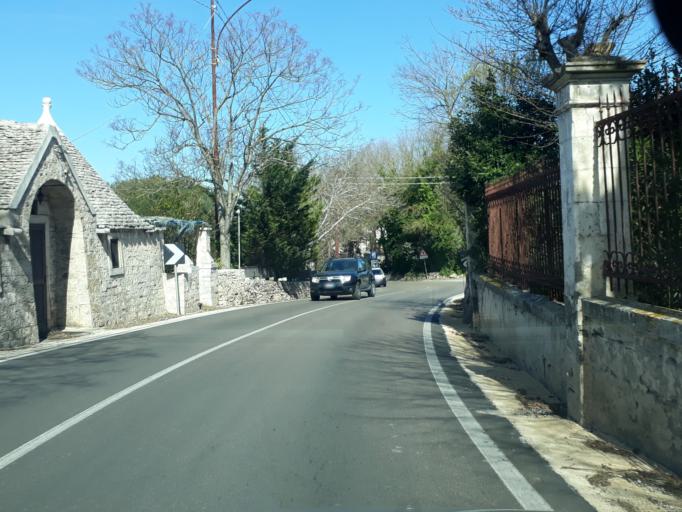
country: IT
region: Apulia
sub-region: Provincia di Brindisi
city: Lamie di Olimpie-Selva
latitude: 40.7988
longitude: 17.3520
